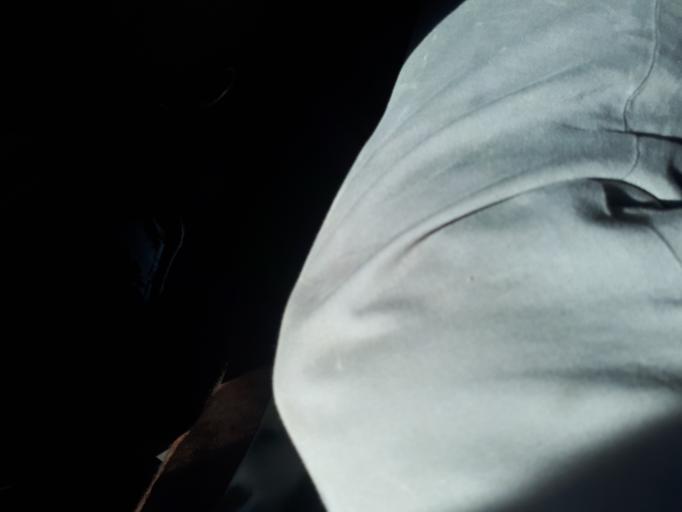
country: VU
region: Sanma
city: Luganville
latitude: -15.5820
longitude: 167.1147
